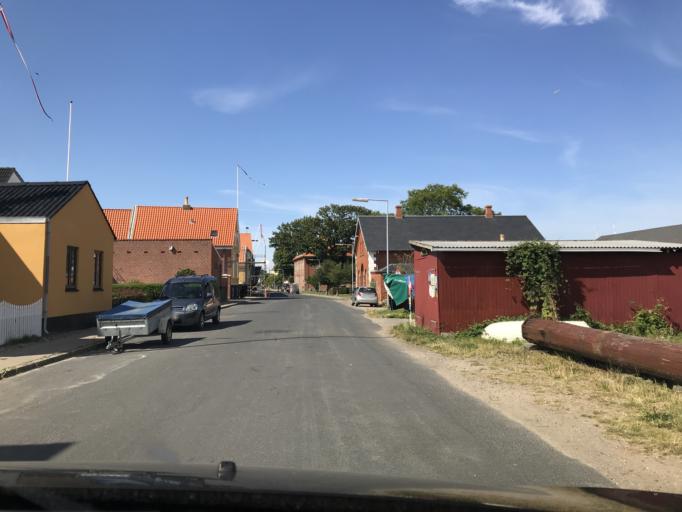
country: DK
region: South Denmark
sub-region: AEro Kommune
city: Marstal
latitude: 54.8536
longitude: 10.5216
